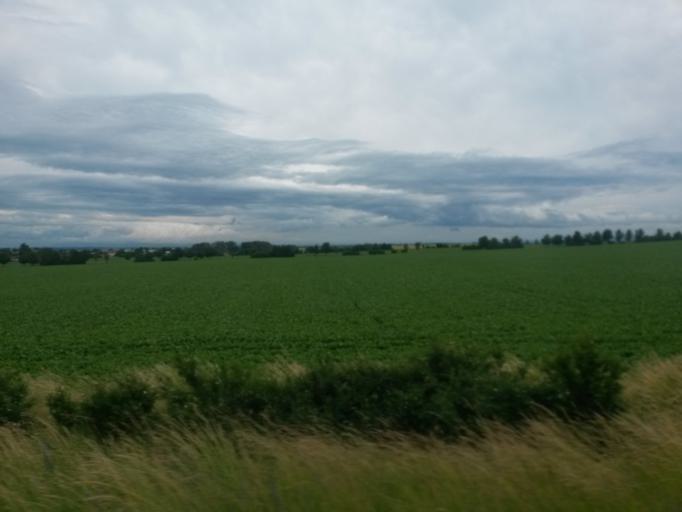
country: CZ
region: Olomoucky
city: Hnevotin
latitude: 49.5601
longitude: 17.1965
